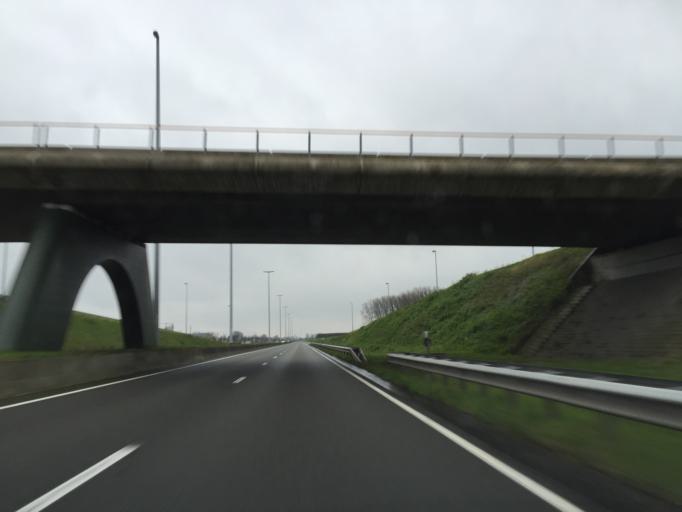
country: BE
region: Flanders
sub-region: Provincie Oost-Vlaanderen
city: Evergem
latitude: 51.1426
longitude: 3.7397
